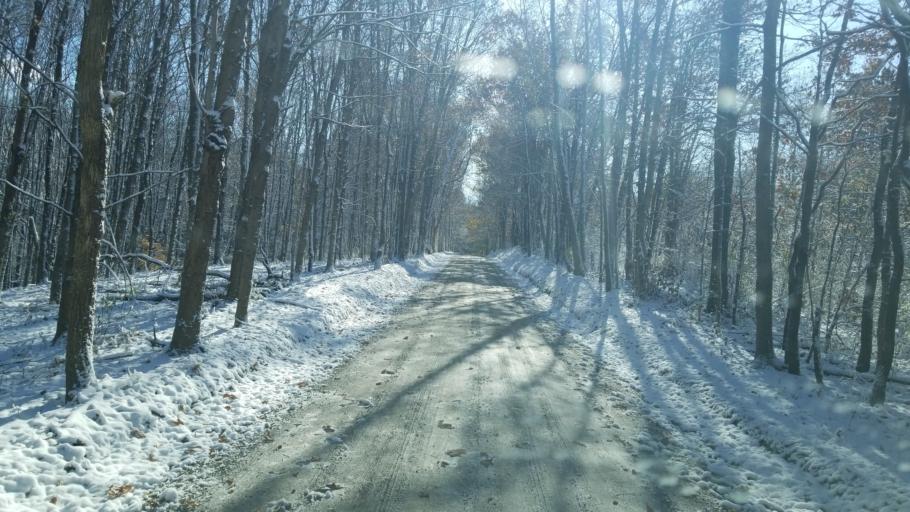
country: US
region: Ohio
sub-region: Licking County
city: Newark
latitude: 40.1496
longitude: -82.3493
